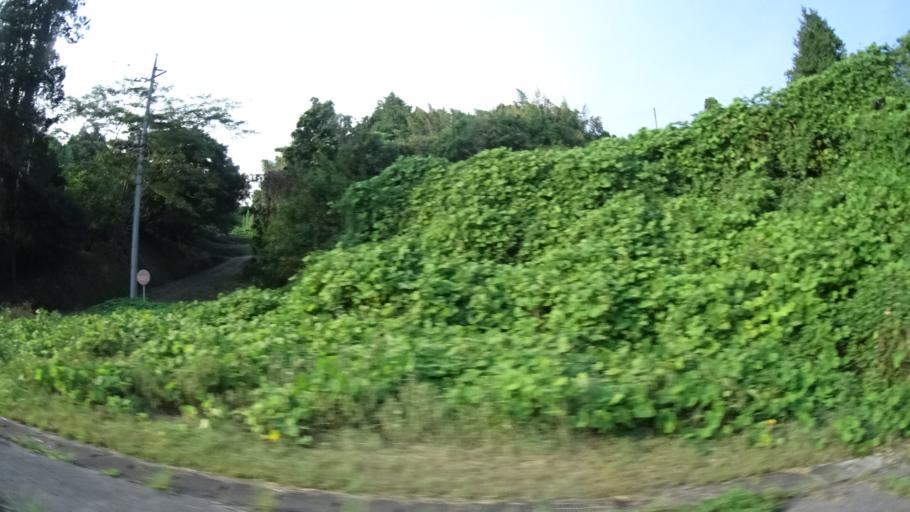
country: JP
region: Tochigi
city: Karasuyama
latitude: 36.6005
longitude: 140.1470
